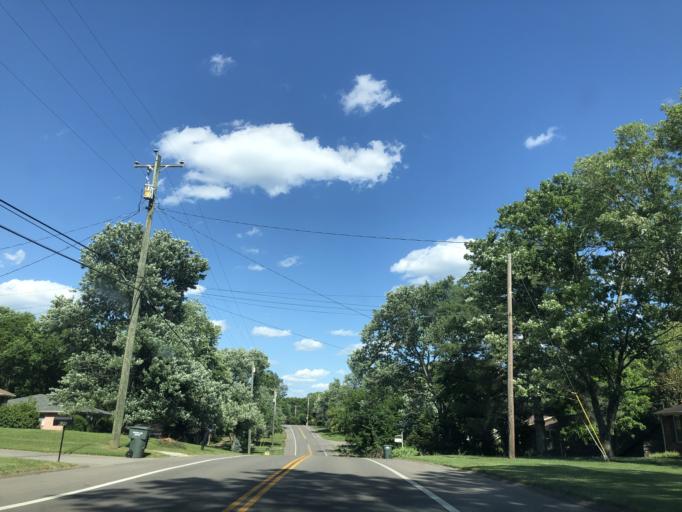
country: US
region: Tennessee
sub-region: Davidson County
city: Belle Meade
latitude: 36.0609
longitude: -86.9297
